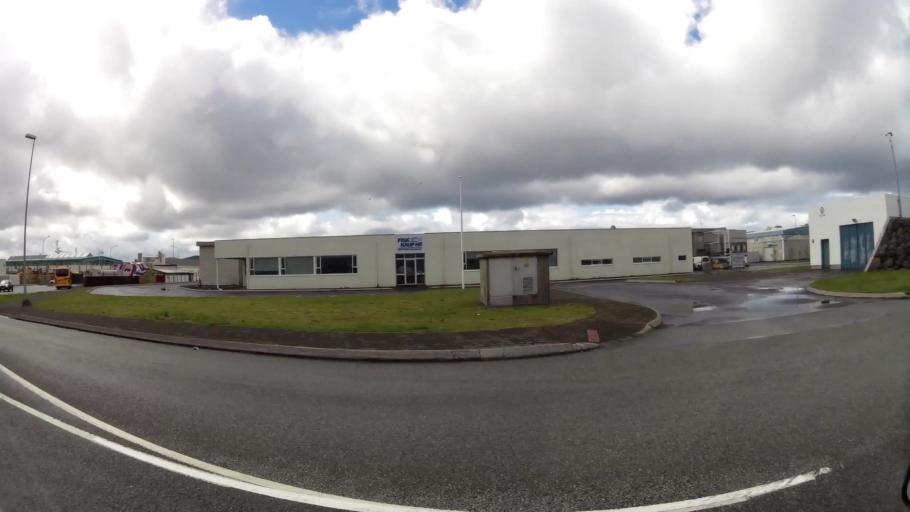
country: IS
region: Capital Region
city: Reykjavik
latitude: 64.1566
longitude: -21.9413
